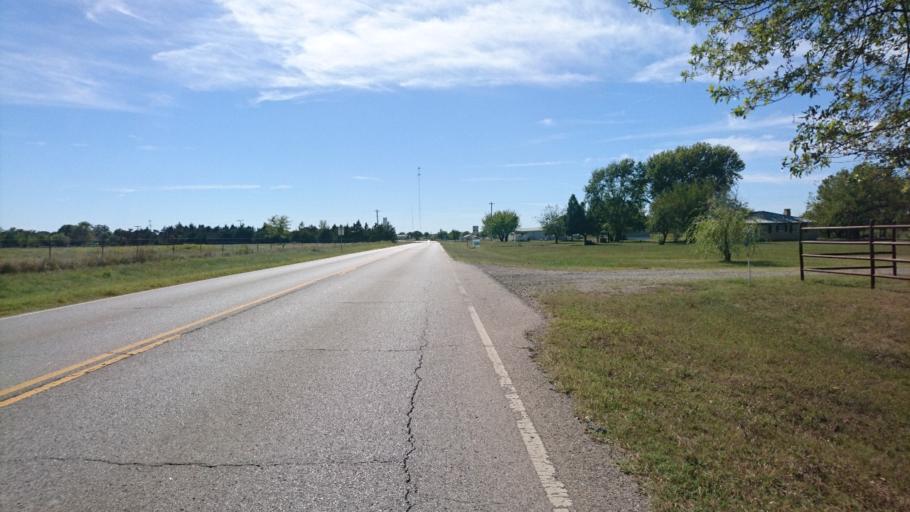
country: US
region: Oklahoma
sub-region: Lincoln County
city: Stroud
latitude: 35.7218
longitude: -96.7589
